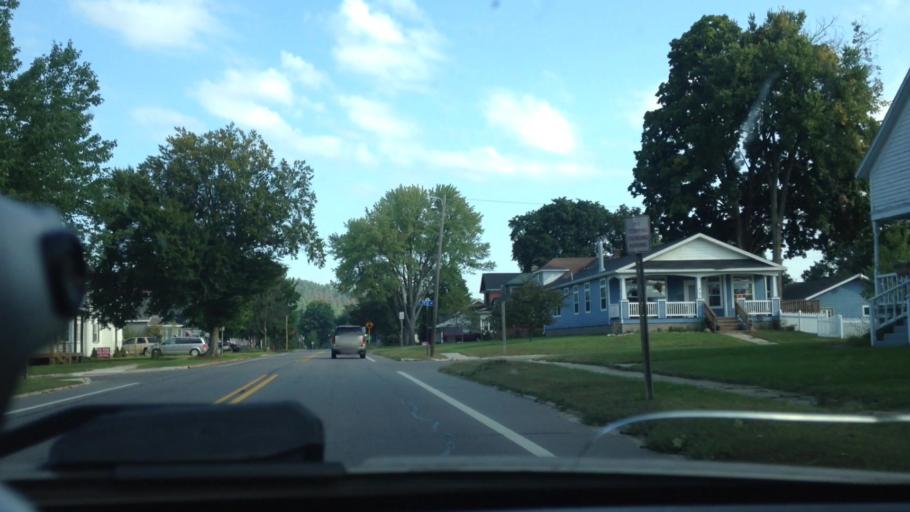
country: US
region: Michigan
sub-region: Dickinson County
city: Norway
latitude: 45.7845
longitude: -87.9098
